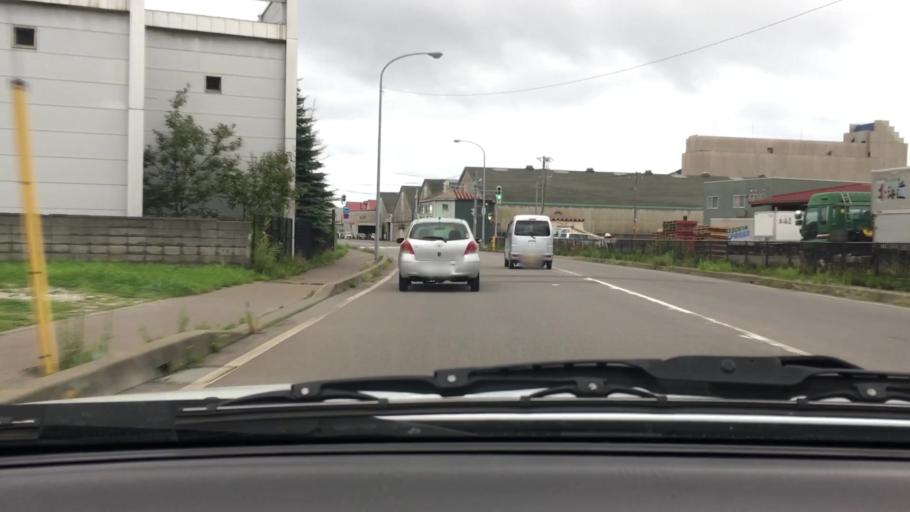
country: JP
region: Hokkaido
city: Hakodate
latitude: 41.7894
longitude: 140.7285
